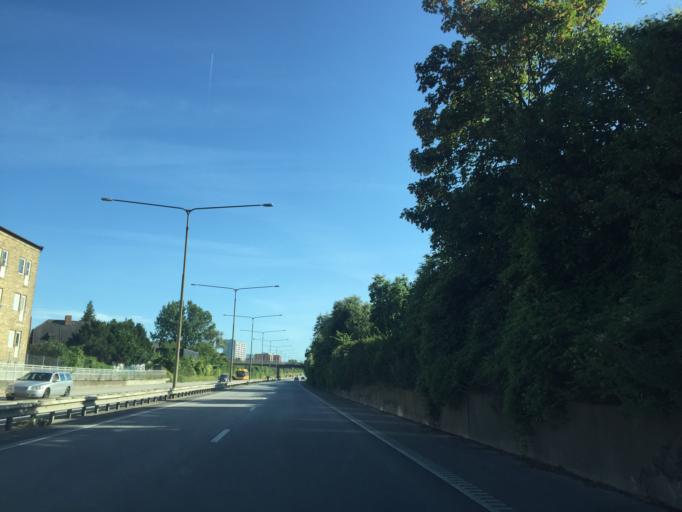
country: SE
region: Skane
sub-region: Malmo
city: Malmoe
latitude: 55.5770
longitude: 13.0049
